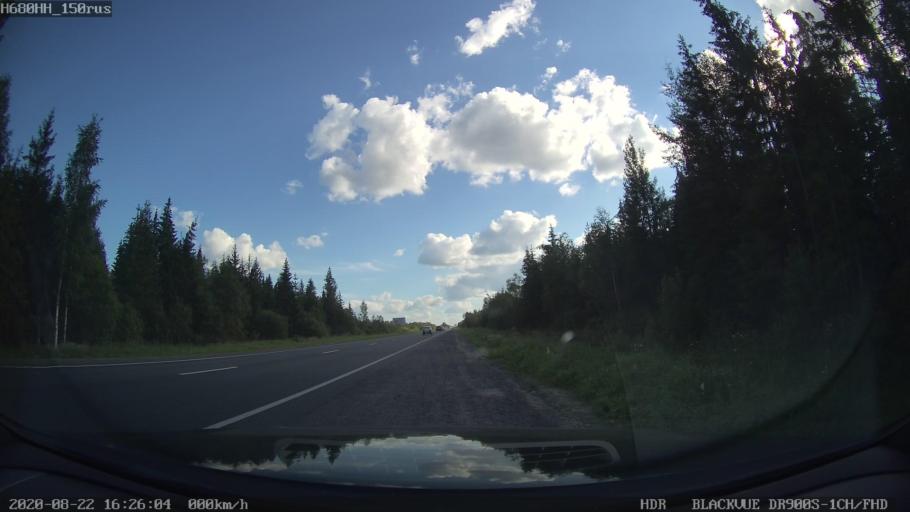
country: RU
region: Tverskaya
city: Rameshki
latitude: 57.3225
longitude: 36.0905
